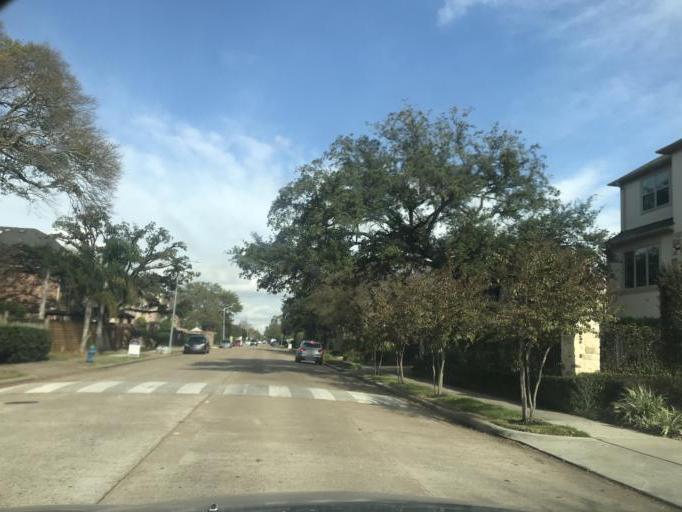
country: US
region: Texas
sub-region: Harris County
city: Hunters Creek Village
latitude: 29.7391
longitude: -95.4886
